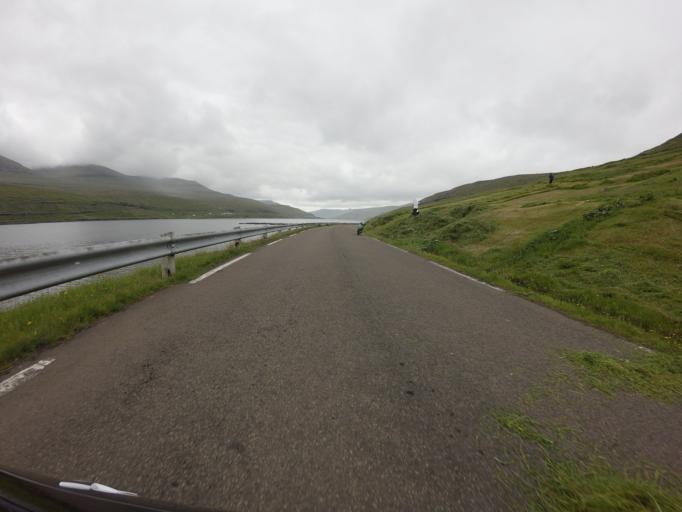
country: FO
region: Eysturoy
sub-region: Eidi
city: Eidi
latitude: 62.2801
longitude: -7.0908
